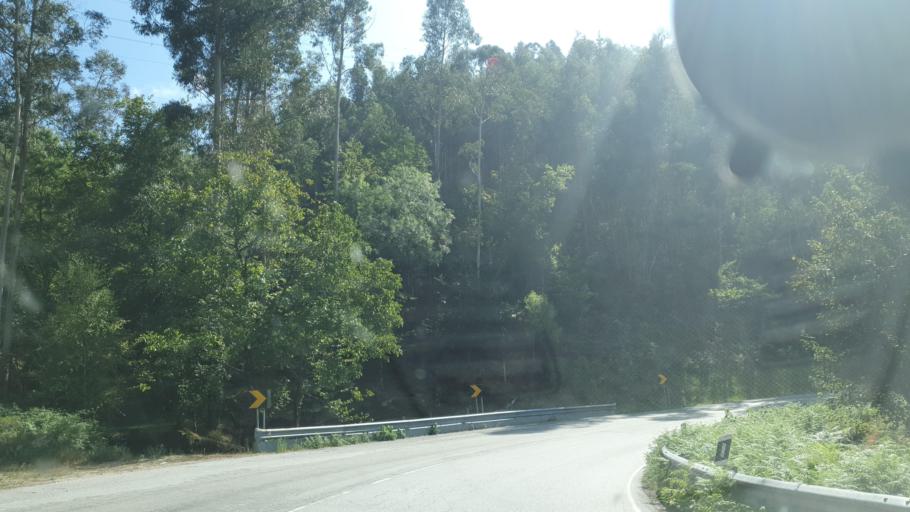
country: PT
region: Braga
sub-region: Vieira do Minho
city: Vieira do Minho
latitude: 41.6727
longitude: -8.1407
